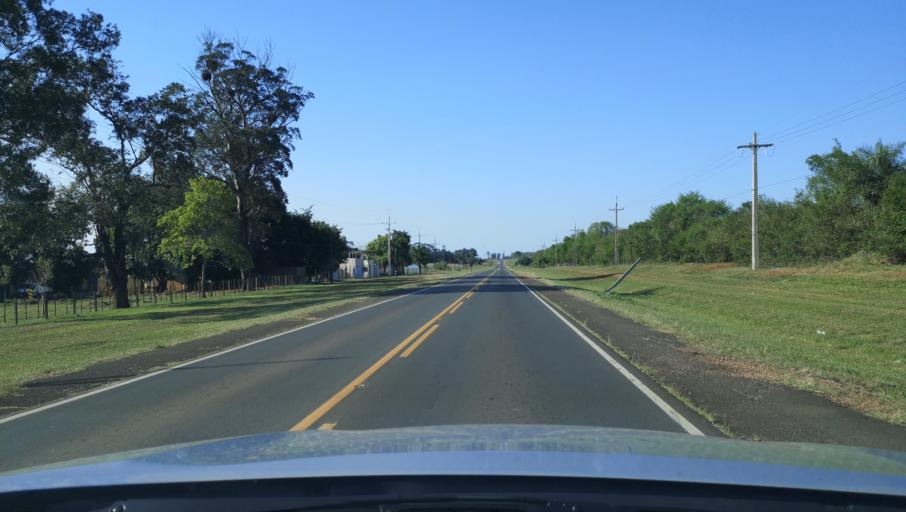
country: PY
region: Misiones
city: Santa Maria
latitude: -26.8217
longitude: -57.0269
